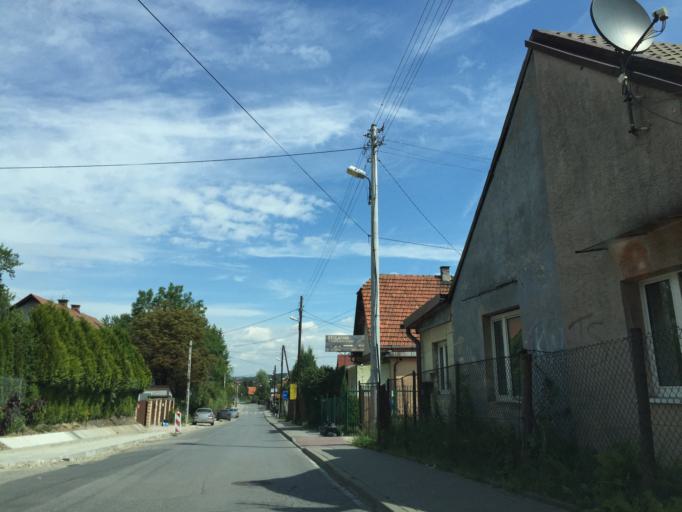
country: PL
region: Lesser Poland Voivodeship
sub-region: Powiat krakowski
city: Modlniczka
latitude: 50.0955
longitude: 19.8827
